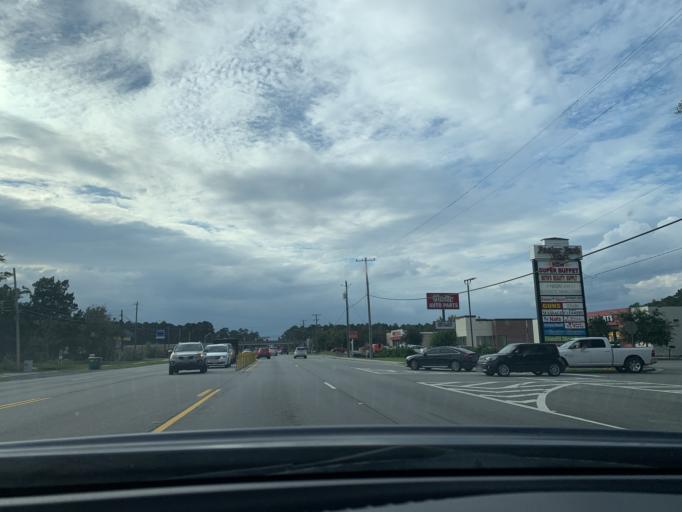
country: US
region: Georgia
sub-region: Chatham County
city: Pooler
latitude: 32.1211
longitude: -81.2636
